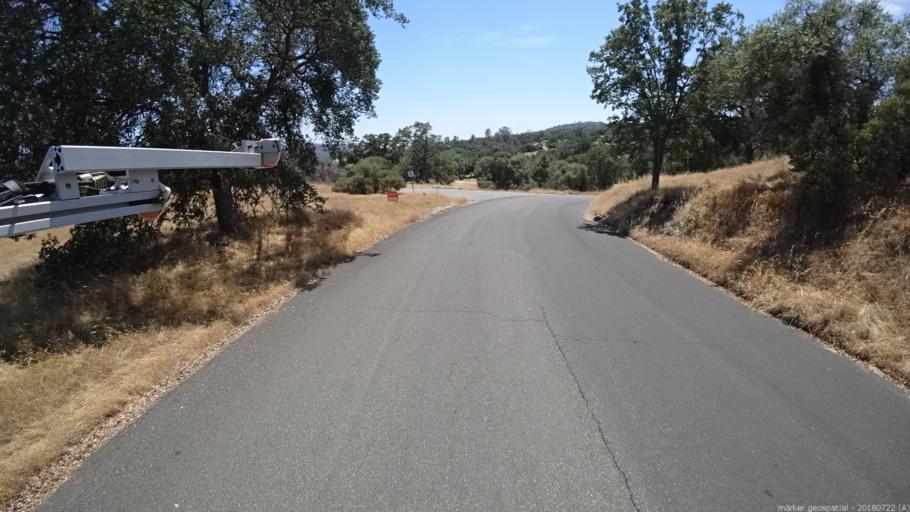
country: US
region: California
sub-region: Madera County
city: Yosemite Lakes
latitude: 37.2195
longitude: -119.7316
